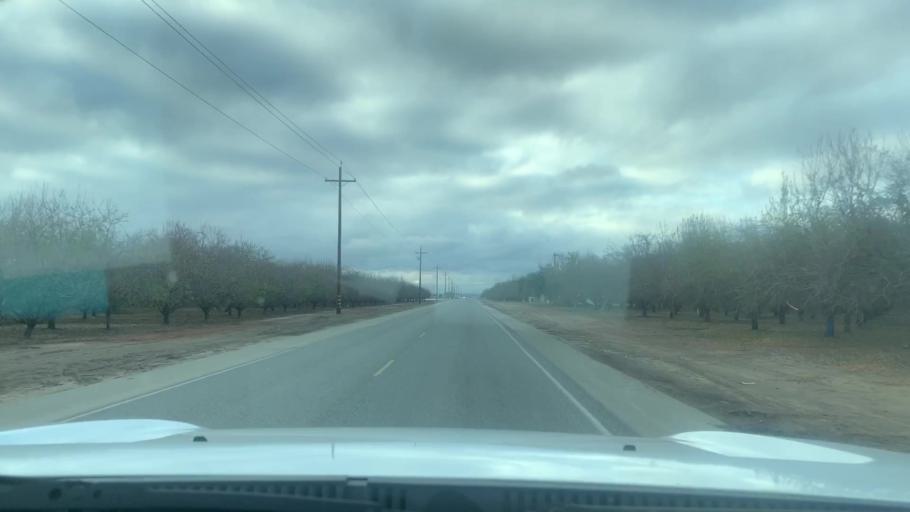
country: US
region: California
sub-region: Kern County
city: Buttonwillow
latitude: 35.5007
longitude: -119.5157
